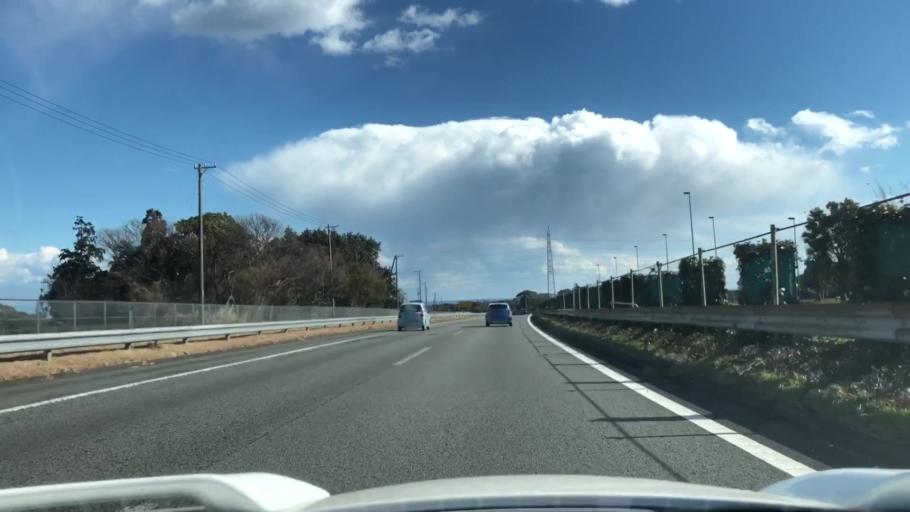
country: JP
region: Shizuoka
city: Shimada
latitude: 34.7580
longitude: 138.1680
